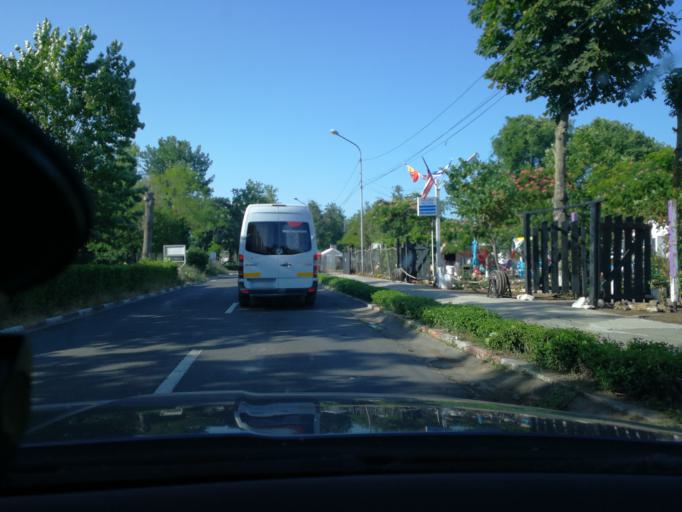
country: RO
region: Constanta
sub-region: Municipiul Mangalia
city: Mangalia
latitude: 43.8479
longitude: 28.5997
